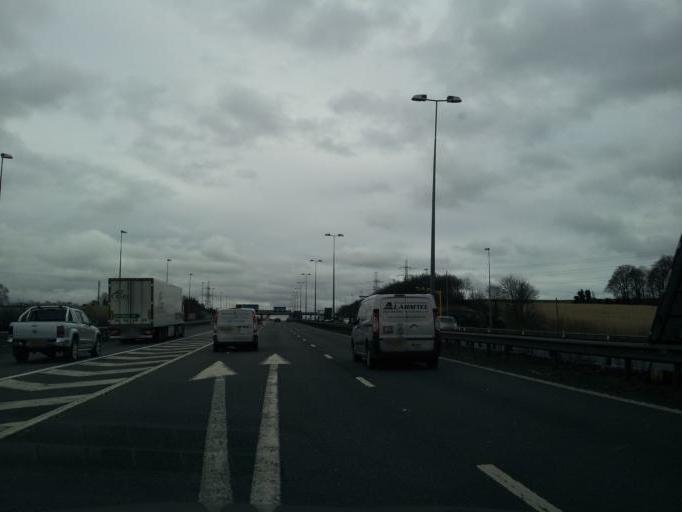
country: GB
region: England
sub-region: Staffordshire
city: Featherstone
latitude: 52.6734
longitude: -2.0809
